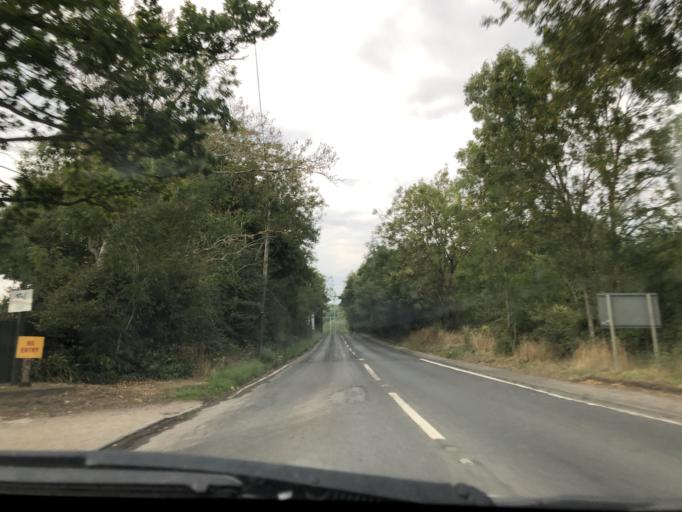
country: GB
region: England
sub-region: Kent
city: Sevenoaks
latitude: 51.2379
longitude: 0.2121
